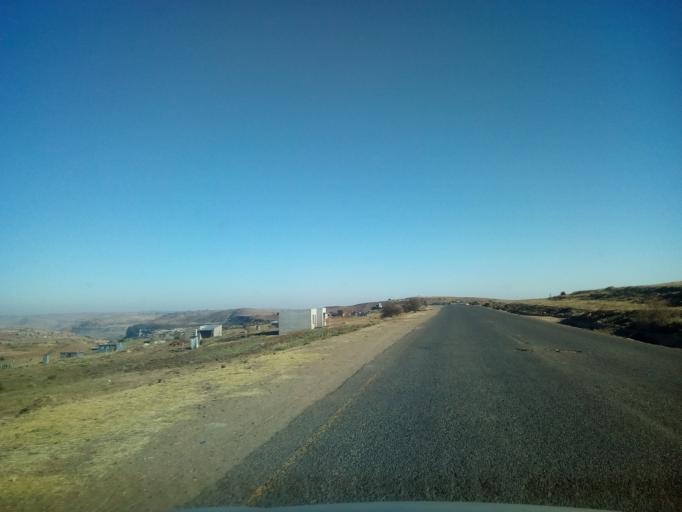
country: LS
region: Berea
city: Teyateyaneng
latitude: -29.2562
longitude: 27.8014
